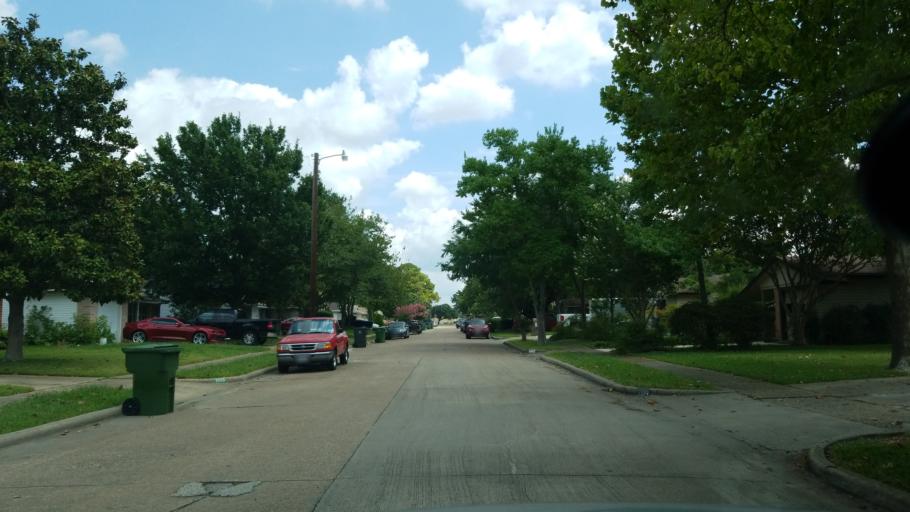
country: US
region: Texas
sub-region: Dallas County
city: Garland
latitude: 32.9226
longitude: -96.6509
